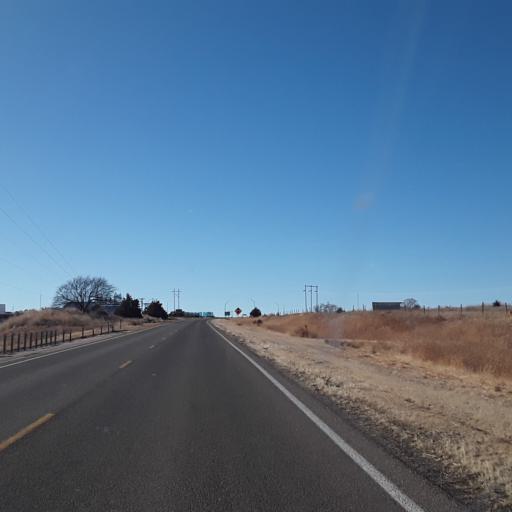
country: US
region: Nebraska
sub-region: Frontier County
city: Stockville
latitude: 40.6571
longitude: -100.6343
